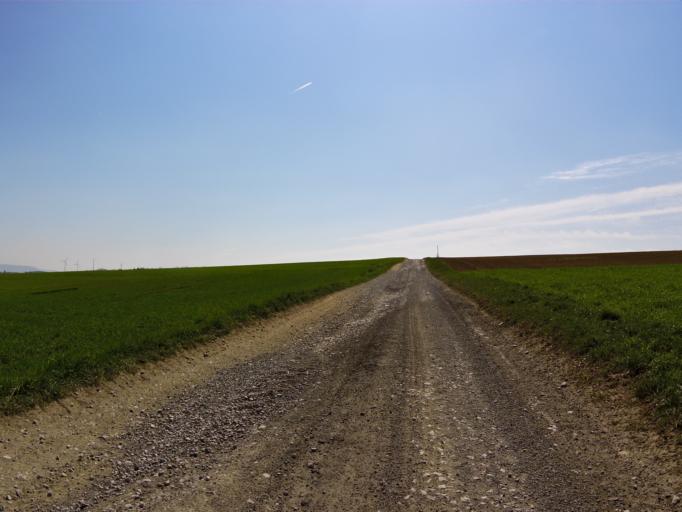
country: DE
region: Bavaria
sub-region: Regierungsbezirk Unterfranken
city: Biebelried
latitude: 49.7892
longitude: 10.0635
